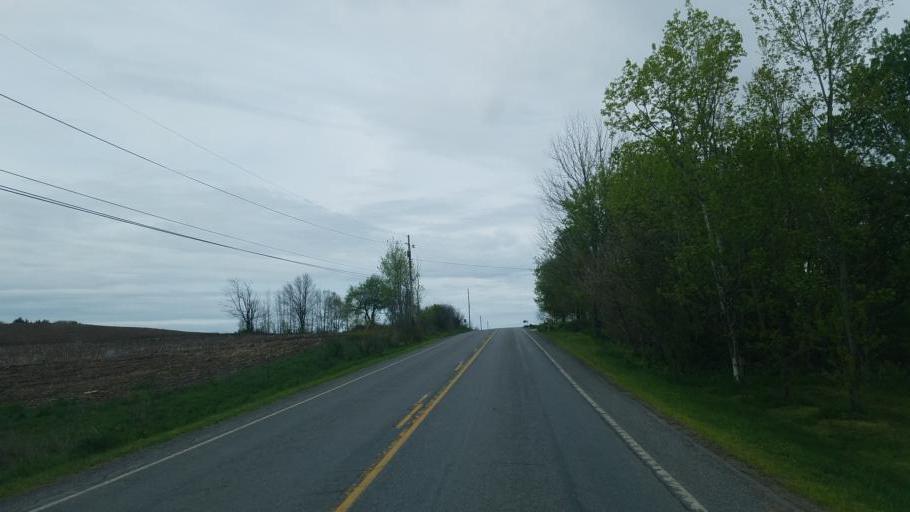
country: US
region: Pennsylvania
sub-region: Tioga County
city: Westfield
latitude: 41.9314
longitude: -77.7231
